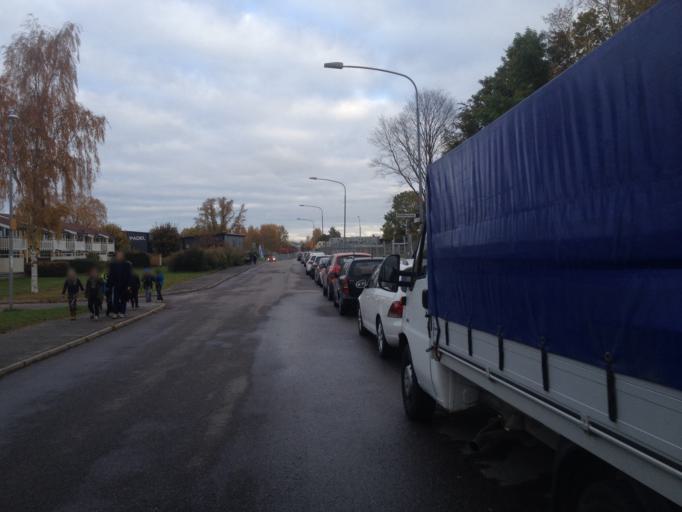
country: SE
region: OEstergoetland
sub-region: Norrkopings Kommun
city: Norrkoping
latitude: 58.5990
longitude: 16.1737
